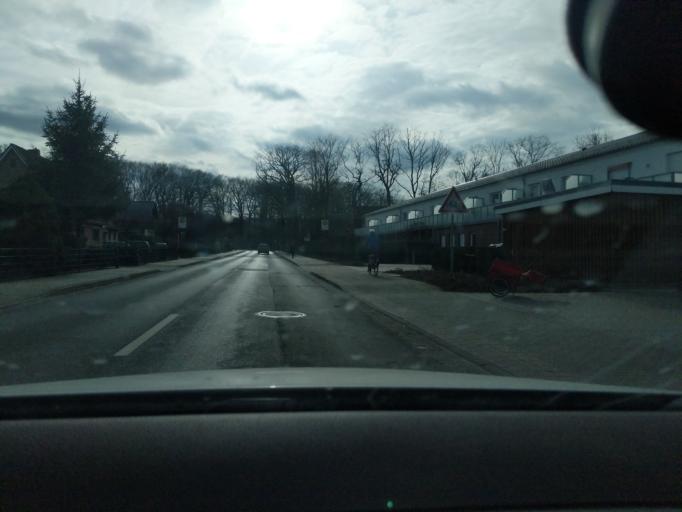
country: DE
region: Lower Saxony
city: Himmelpforten
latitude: 53.6164
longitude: 9.3145
